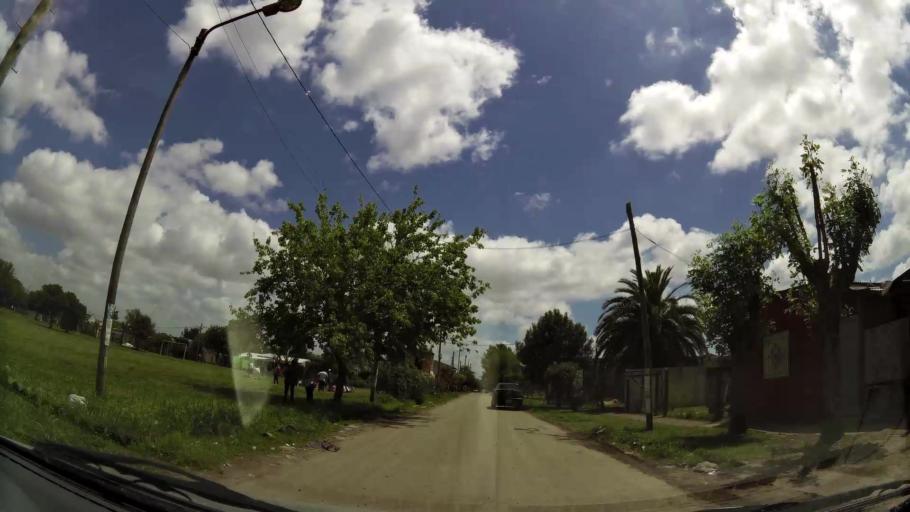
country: AR
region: Buenos Aires
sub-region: Partido de Quilmes
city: Quilmes
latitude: -34.8276
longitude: -58.2411
